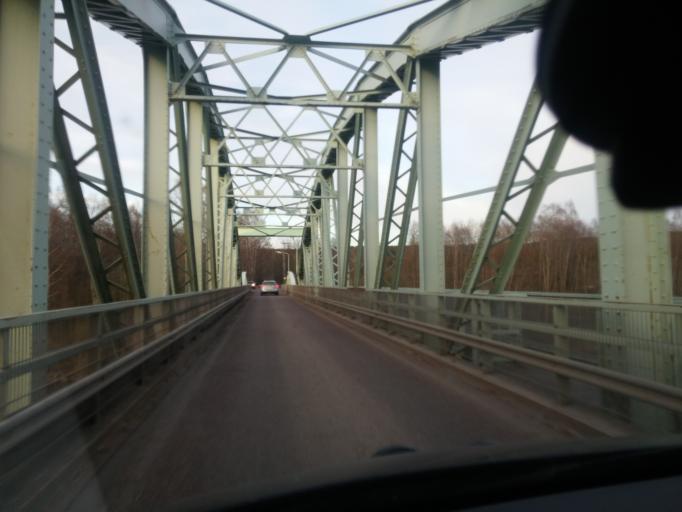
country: SE
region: Dalarna
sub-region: Borlange Kommun
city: Borlaenge
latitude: 60.5382
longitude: 15.4175
